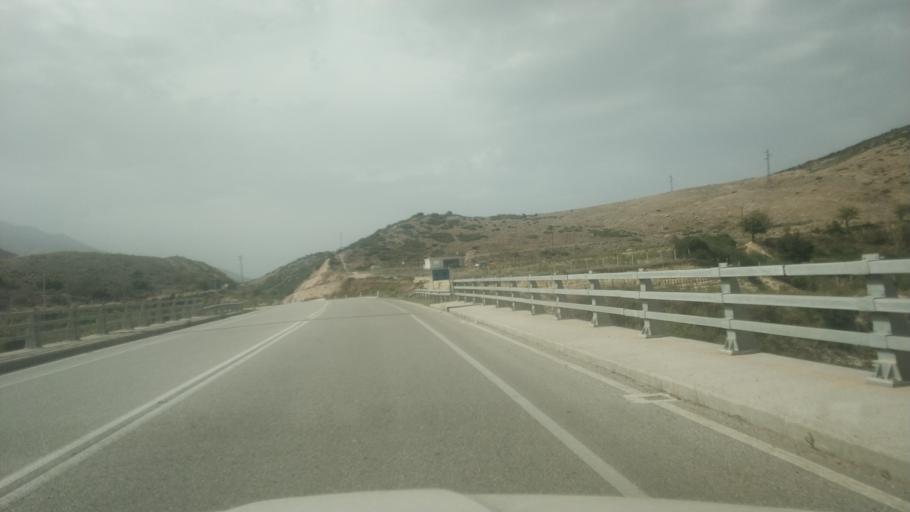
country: AL
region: Gjirokaster
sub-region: Rrethi i Tepelenes
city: Memaliaj
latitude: 40.3635
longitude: 19.9248
